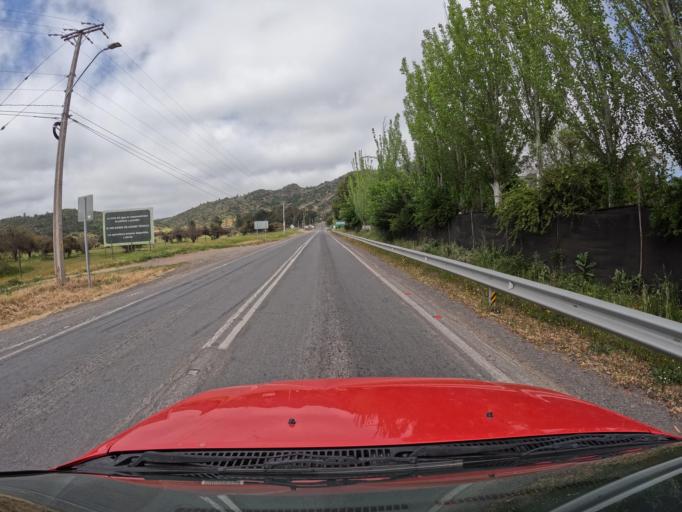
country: CL
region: O'Higgins
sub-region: Provincia de Colchagua
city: Santa Cruz
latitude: -34.6575
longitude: -71.4100
